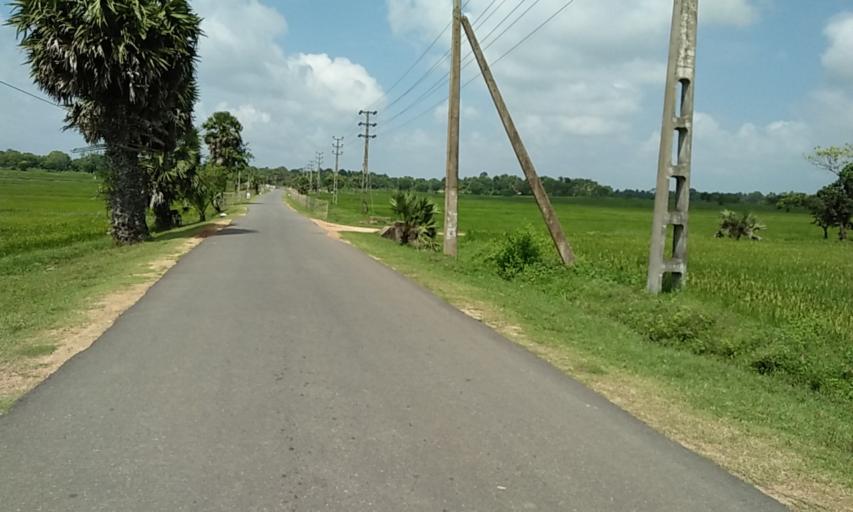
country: LK
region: Eastern Province
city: Ampara
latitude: 7.3390
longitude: 81.7423
